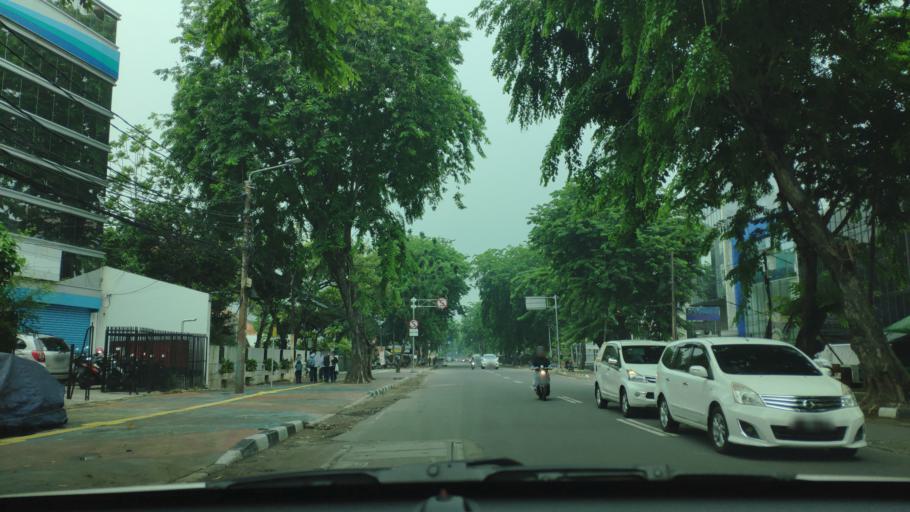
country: ID
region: Jakarta Raya
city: Jakarta
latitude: -6.1659
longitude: 106.8135
